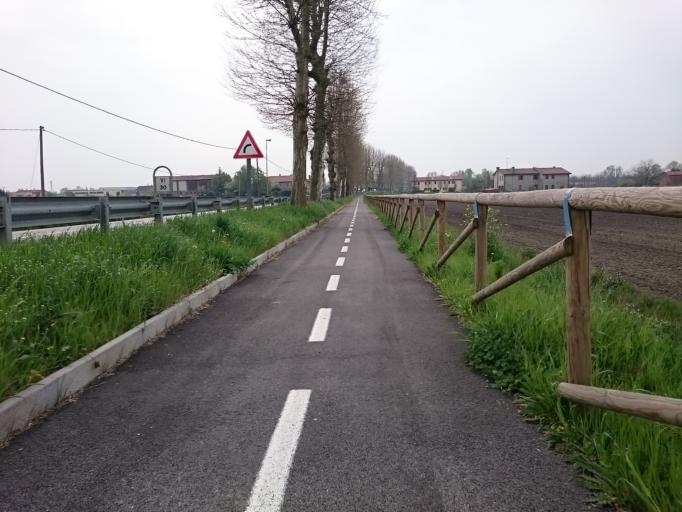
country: IT
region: Veneto
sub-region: Provincia di Padova
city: Anguillara Veneta
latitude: 45.1549
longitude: 11.8766
